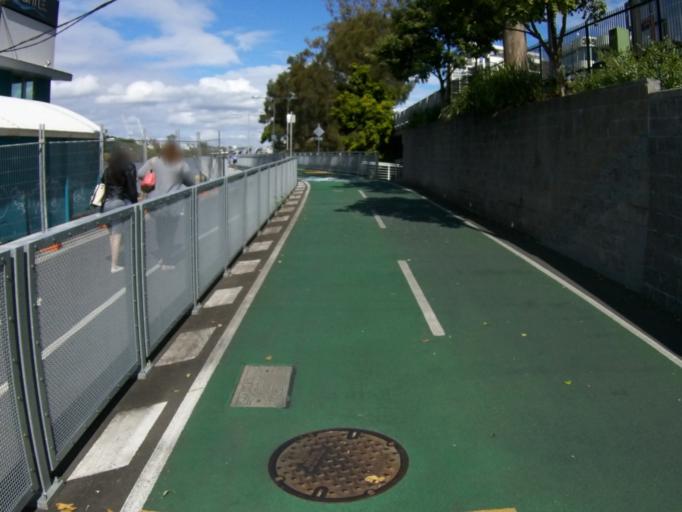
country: AU
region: Queensland
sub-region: Brisbane
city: Milton
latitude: -27.4745
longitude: 153.0039
